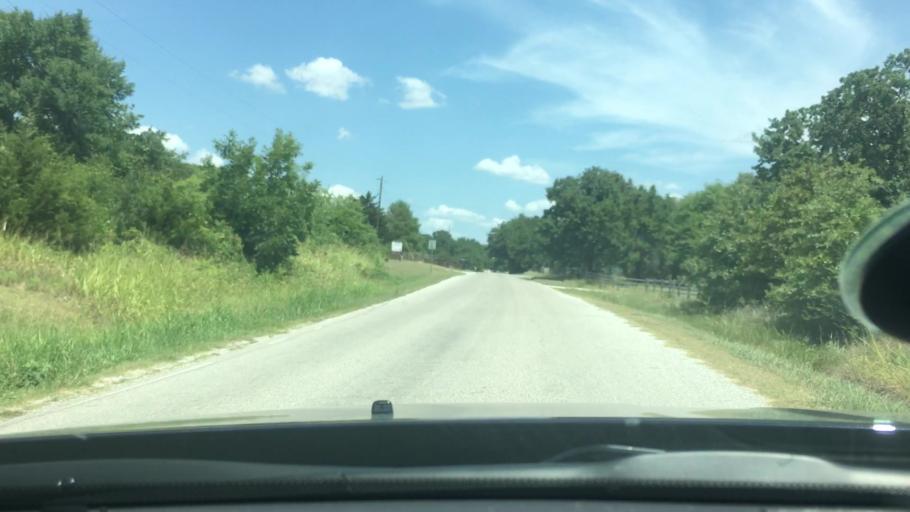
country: US
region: Oklahoma
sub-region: Carter County
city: Ardmore
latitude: 34.0616
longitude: -97.1957
